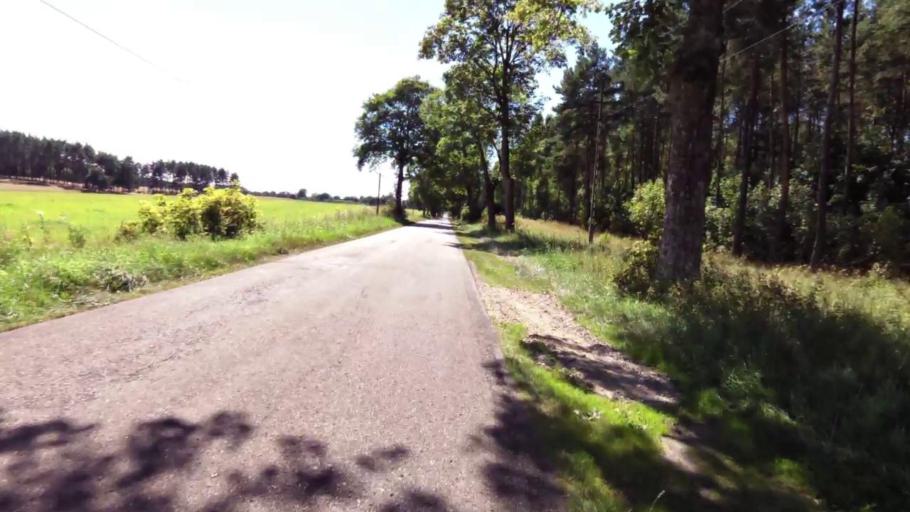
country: PL
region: West Pomeranian Voivodeship
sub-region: Powiat szczecinecki
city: Bialy Bor
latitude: 53.8812
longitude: 16.8056
